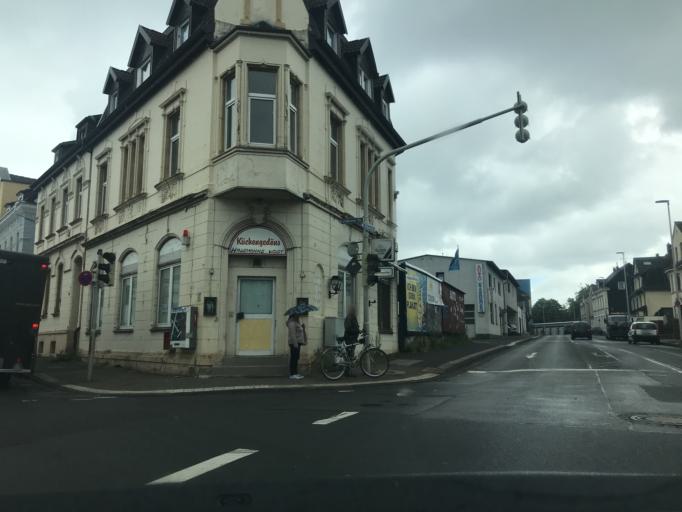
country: DE
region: North Rhine-Westphalia
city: Haan
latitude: 51.1888
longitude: 7.0478
